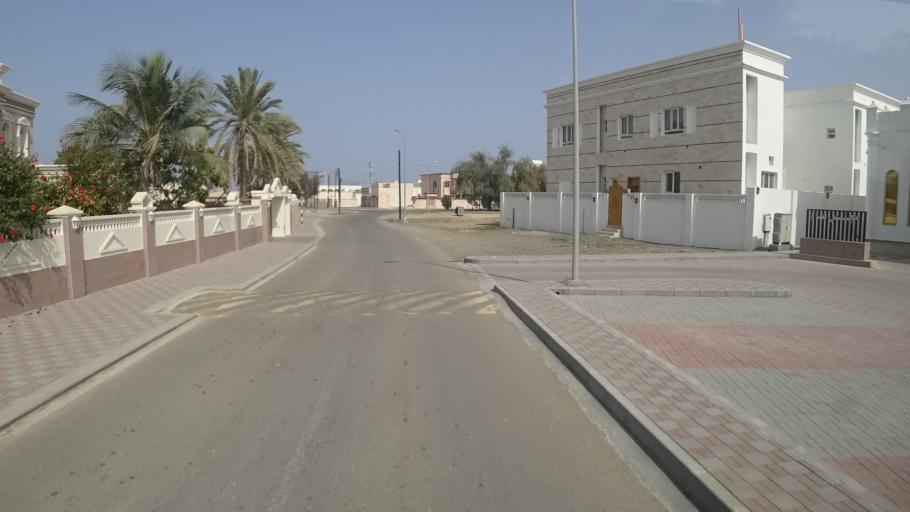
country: OM
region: Al Batinah
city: Saham
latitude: 24.2314
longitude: 56.8307
